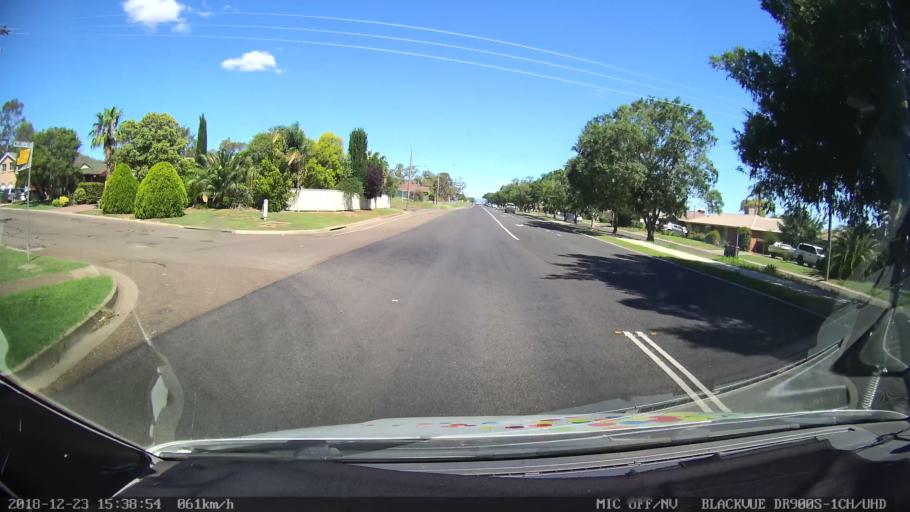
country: AU
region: New South Wales
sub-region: Tamworth Municipality
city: Tamworth
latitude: -31.0619
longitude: 150.8999
